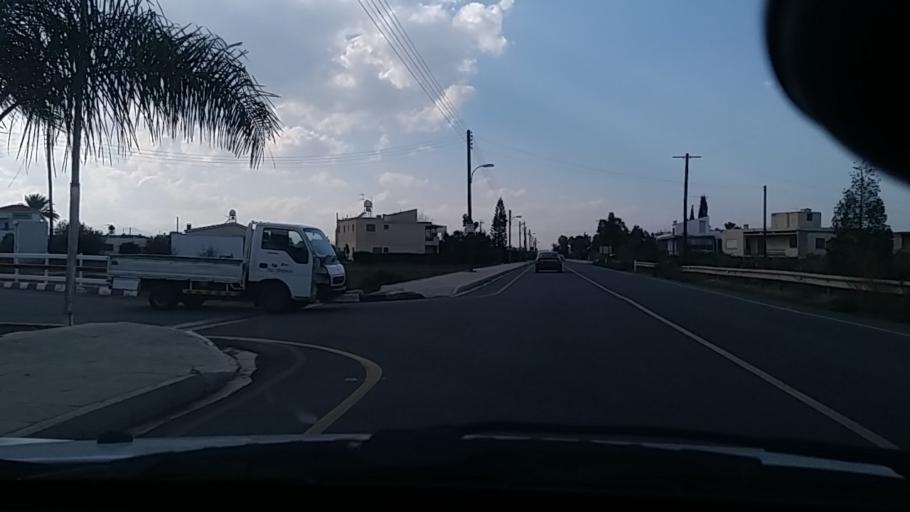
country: CY
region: Lefkosia
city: Akaki
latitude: 35.1372
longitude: 33.1346
